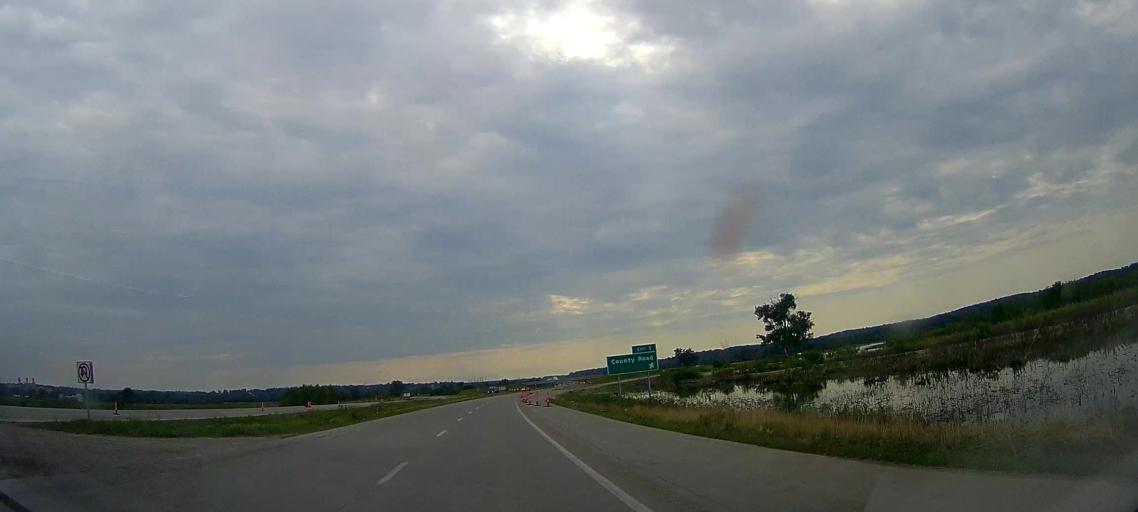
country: US
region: Iowa
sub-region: Pottawattamie County
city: Carter Lake
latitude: 41.3467
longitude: -95.9278
